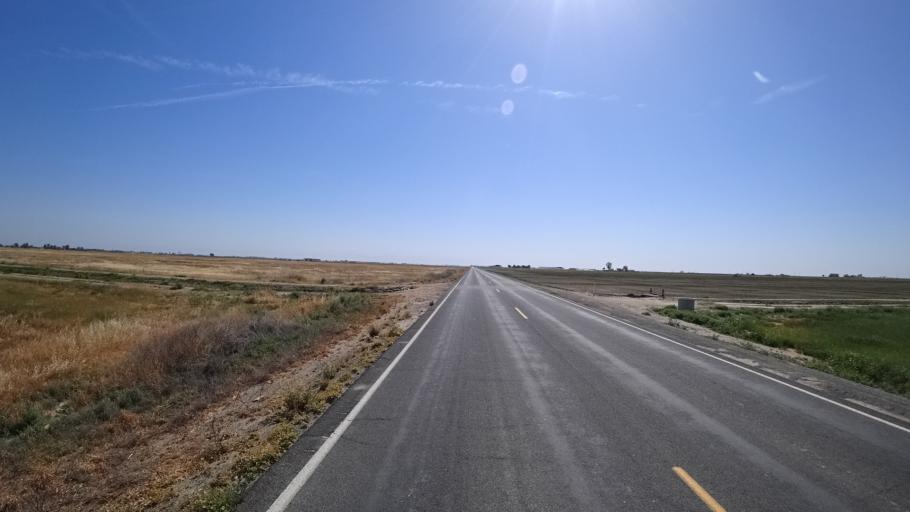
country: US
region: California
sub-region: Kings County
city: Stratford
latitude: 36.2113
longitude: -119.7730
